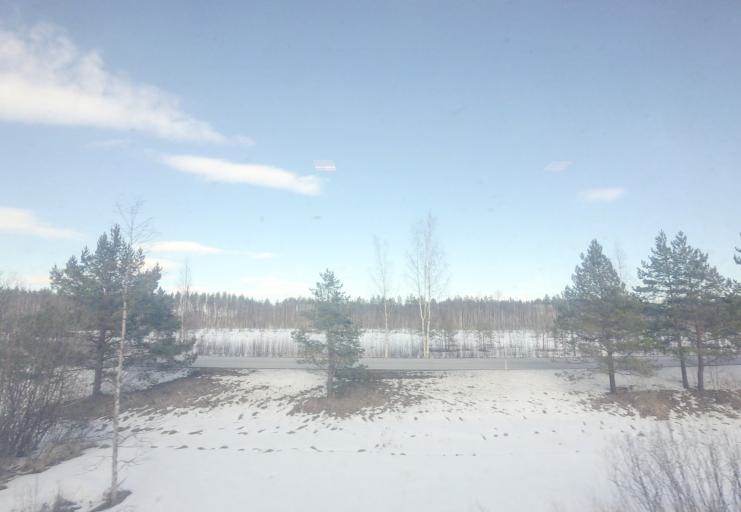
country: FI
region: Southern Savonia
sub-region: Savonlinna
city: Punkaharju
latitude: 61.7877
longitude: 29.3445
